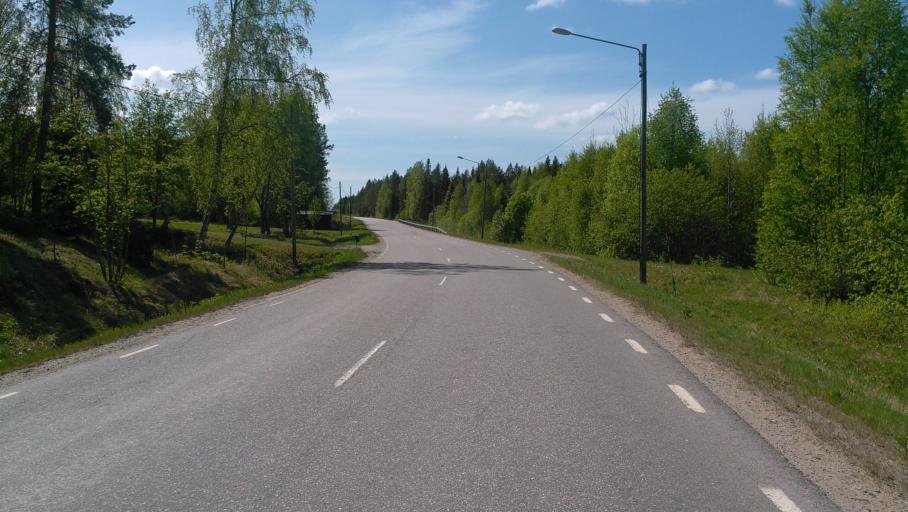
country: SE
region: Vaesterbotten
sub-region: Umea Kommun
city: Roback
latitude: 63.8632
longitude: 20.0126
